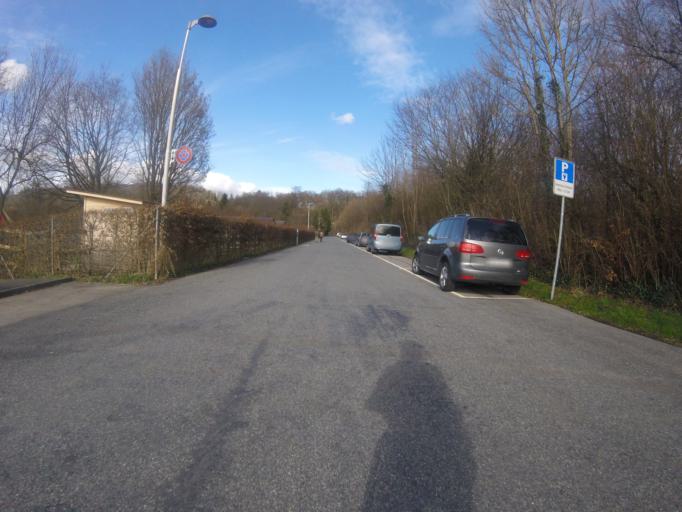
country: CH
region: Bern
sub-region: Bern-Mittelland District
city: Wohlen
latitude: 46.9636
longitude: 7.3844
